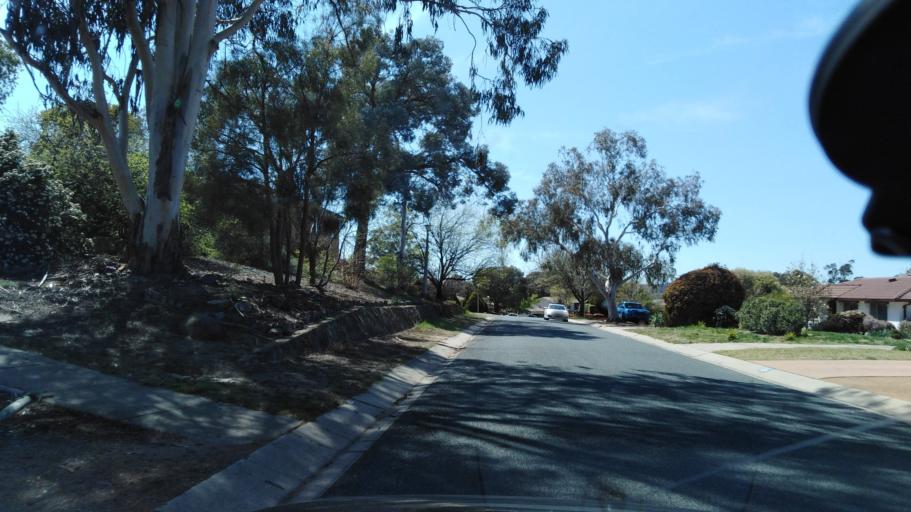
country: AU
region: Australian Capital Territory
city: Forrest
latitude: -35.3502
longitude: 149.0342
